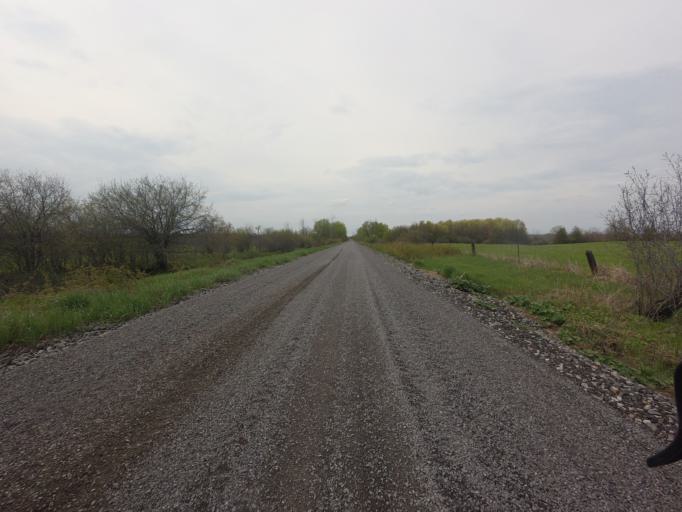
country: CA
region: Ontario
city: Carleton Place
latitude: 45.1971
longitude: -76.1655
